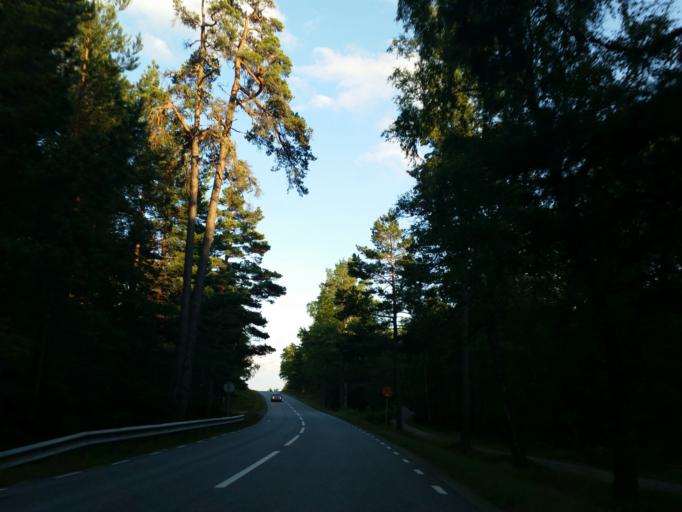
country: SE
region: Stockholm
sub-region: Sodertalje Kommun
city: Soedertaelje
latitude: 59.2328
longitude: 17.5487
